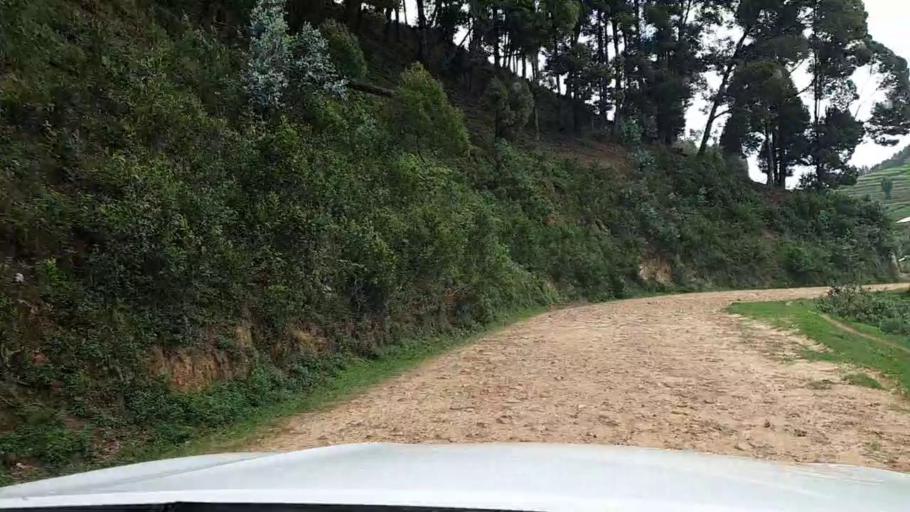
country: RW
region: Western Province
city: Kibuye
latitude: -2.2898
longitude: 29.3687
